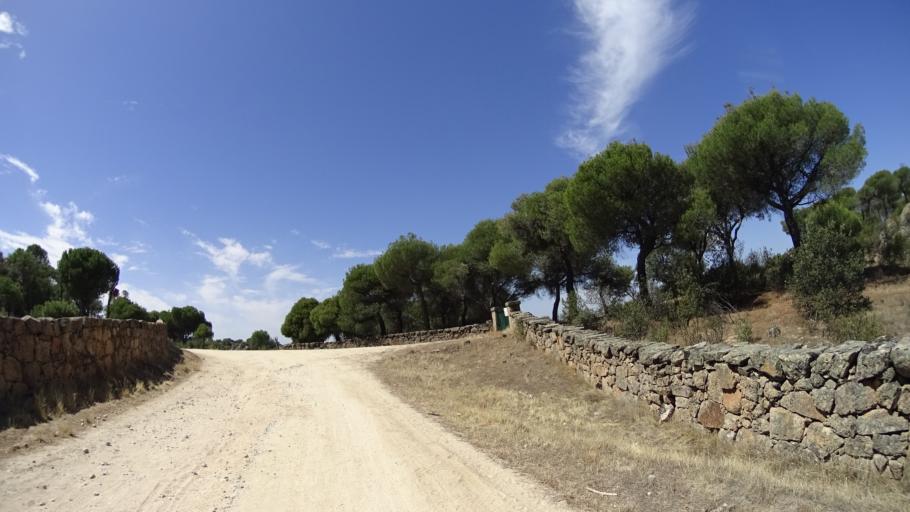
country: ES
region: Madrid
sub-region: Provincia de Madrid
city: Torrelodones
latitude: 40.5649
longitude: -3.9389
